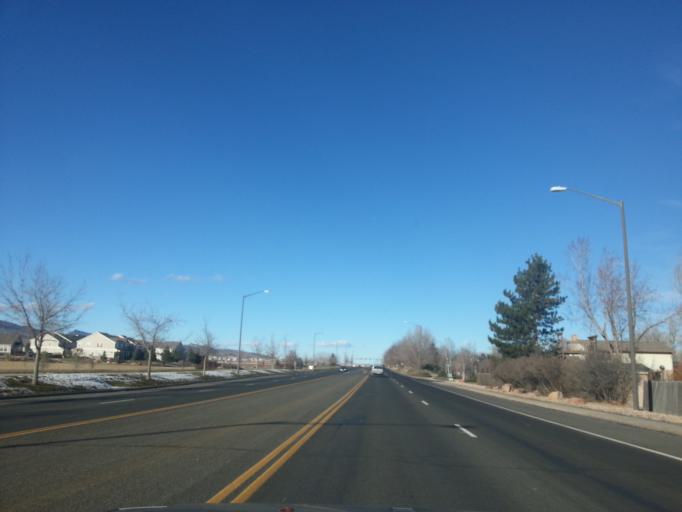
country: US
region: Colorado
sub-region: Larimer County
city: Loveland
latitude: 40.4240
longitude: -105.1156
